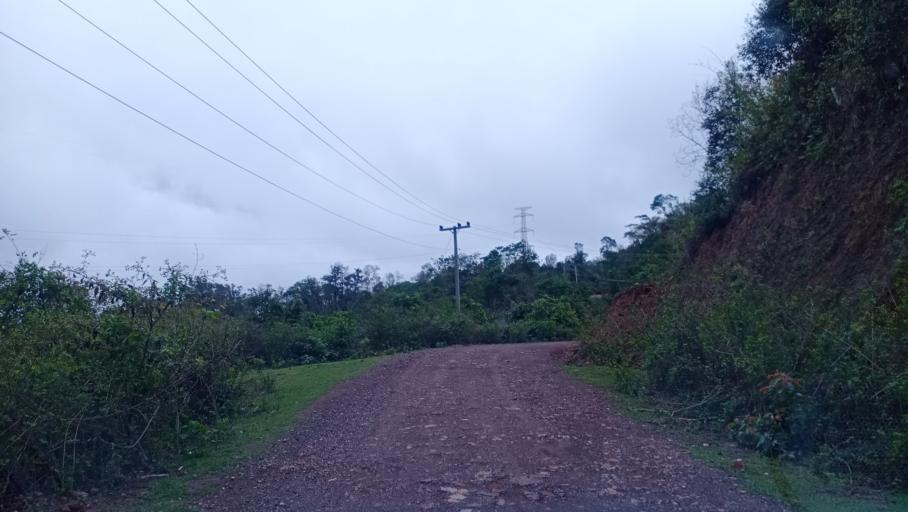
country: LA
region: Phongsali
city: Phongsali
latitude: 21.3433
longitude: 102.0892
